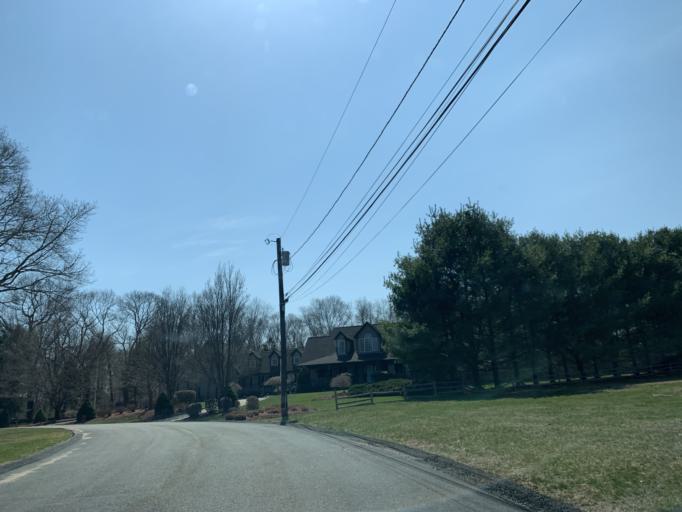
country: US
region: Rhode Island
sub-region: Kent County
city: East Greenwich
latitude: 41.6312
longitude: -71.4342
